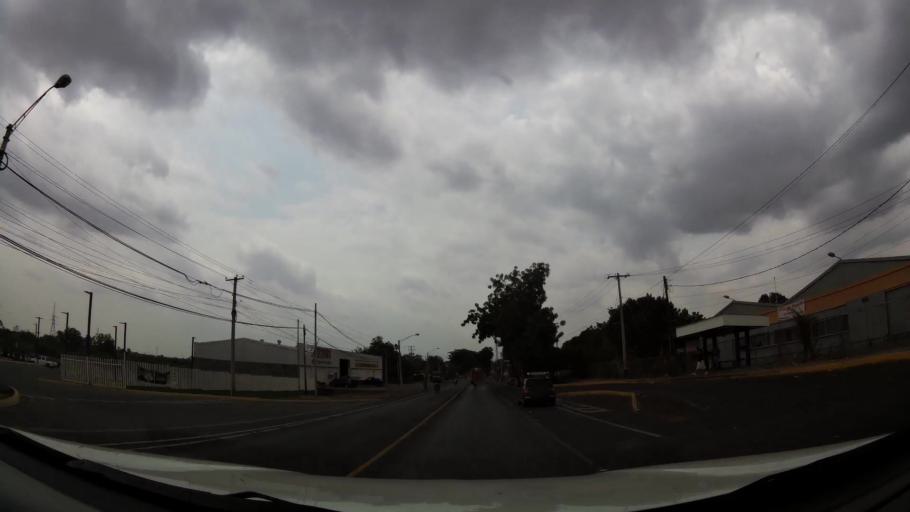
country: NI
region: Leon
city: Leon
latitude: 12.4598
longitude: -86.8678
